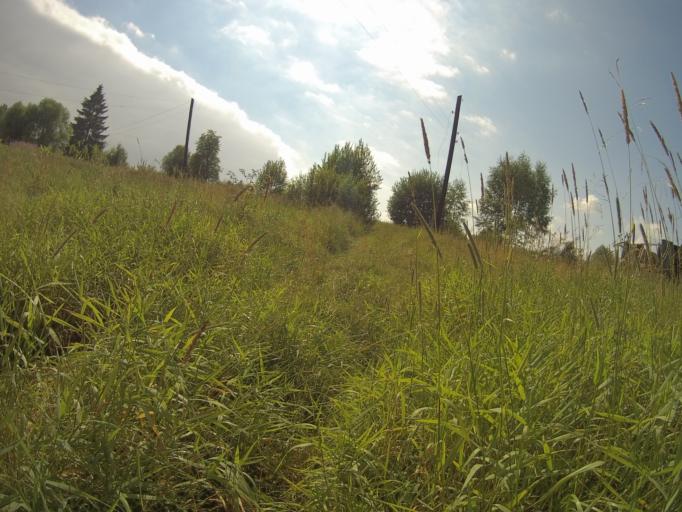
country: RU
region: Vladimir
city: Vorsha
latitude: 56.0039
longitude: 40.1983
